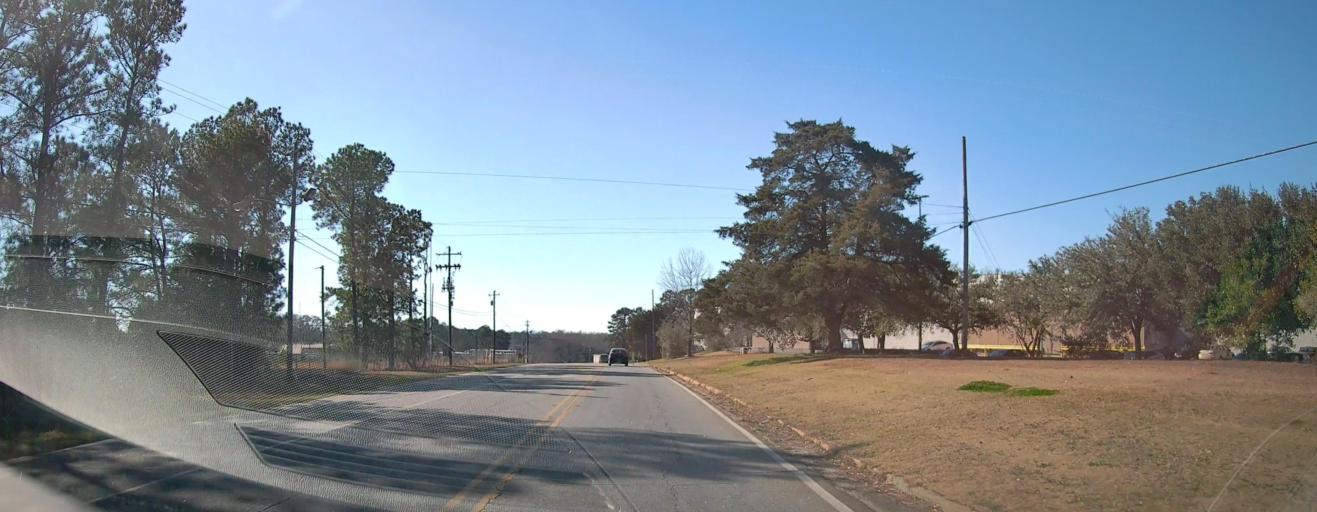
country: US
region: Georgia
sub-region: Sumter County
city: Americus
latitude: 32.0592
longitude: -84.2015
